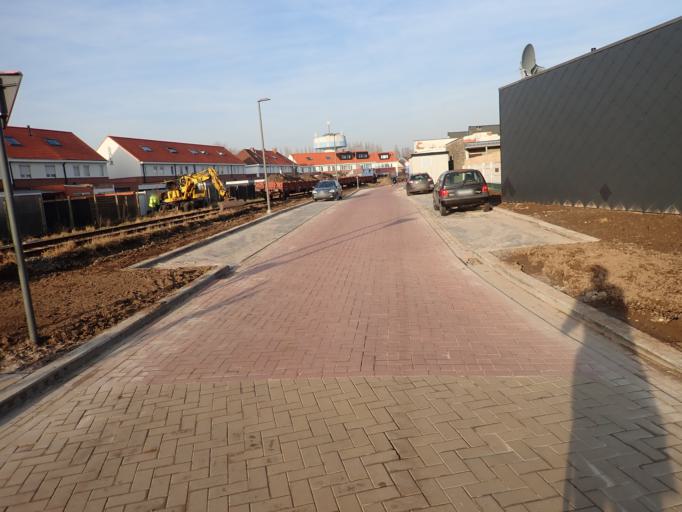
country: BE
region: Flanders
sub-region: Provincie Antwerpen
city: Sint-Amands
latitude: 51.0554
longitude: 4.2098
